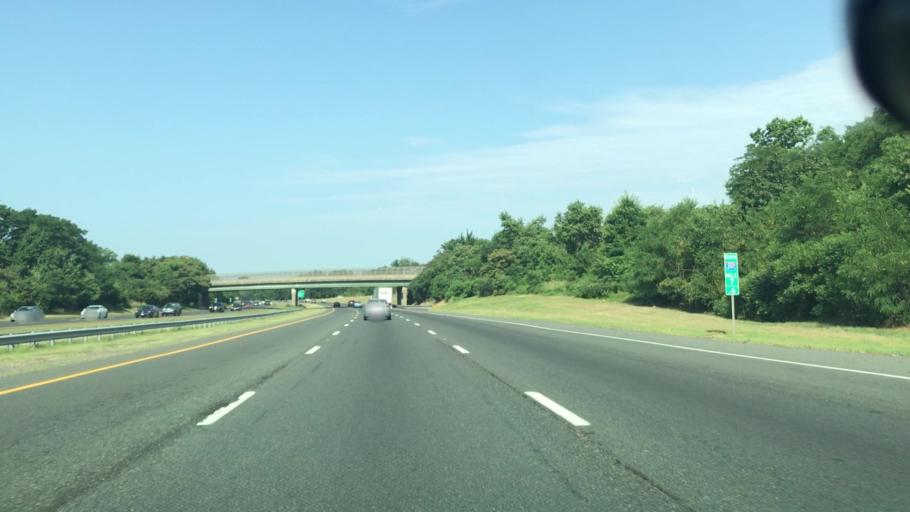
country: US
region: New Jersey
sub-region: Middlesex County
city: Society Hill
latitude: 40.5570
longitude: -74.4681
